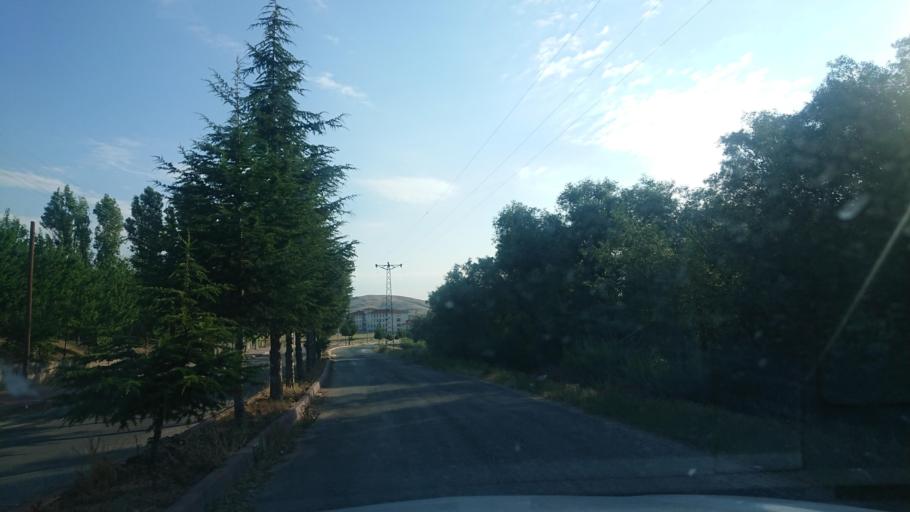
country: TR
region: Aksaray
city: Ortakoy
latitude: 38.7499
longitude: 34.0553
